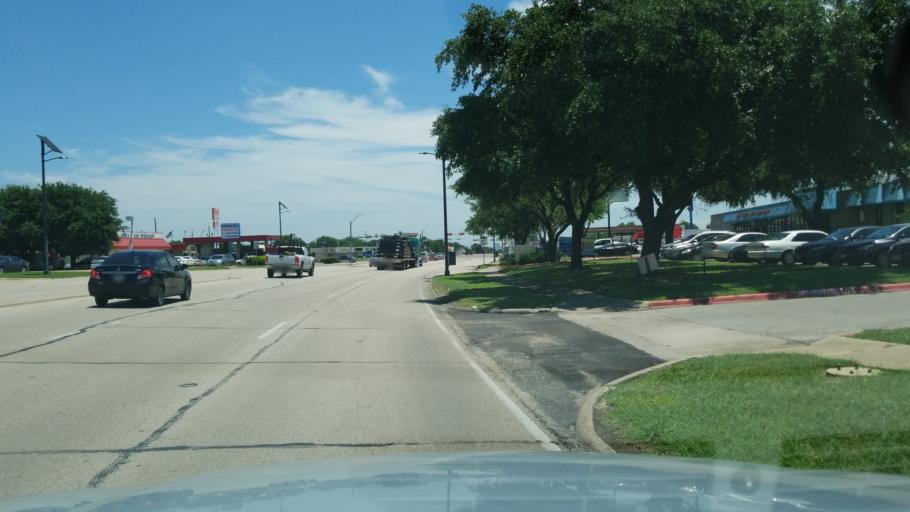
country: US
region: Texas
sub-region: Dallas County
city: Irving
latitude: 32.8094
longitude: -96.9242
